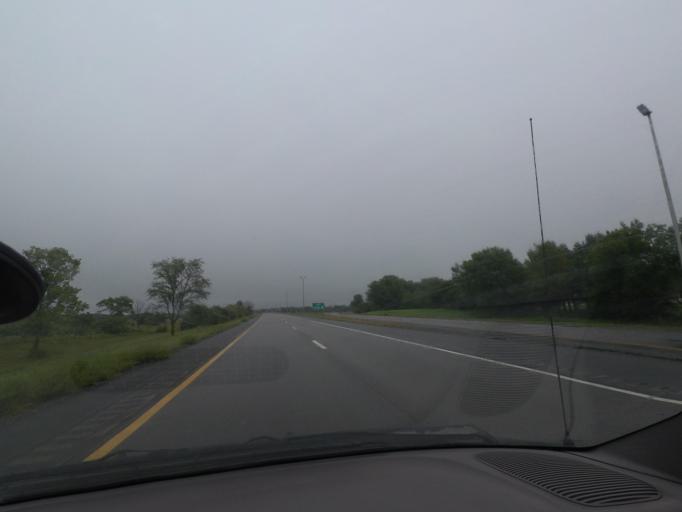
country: US
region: Illinois
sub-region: Macon County
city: Harristown
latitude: 39.8368
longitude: -89.0519
